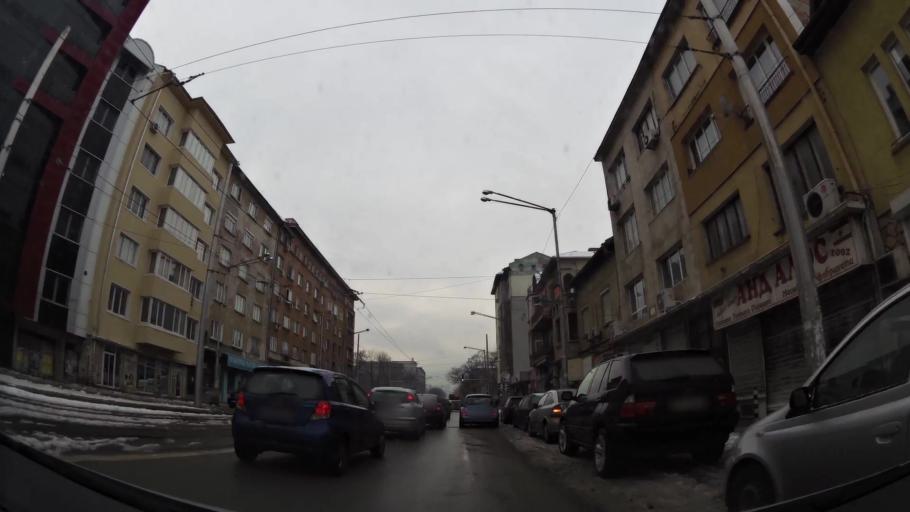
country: BG
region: Sofia-Capital
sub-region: Stolichna Obshtina
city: Sofia
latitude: 42.7102
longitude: 23.3185
